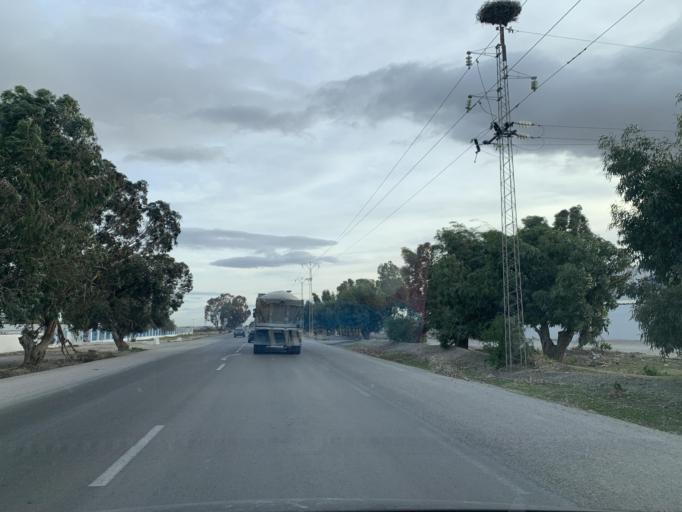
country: TN
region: Susah
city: Harqalah
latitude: 36.1067
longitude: 10.3872
